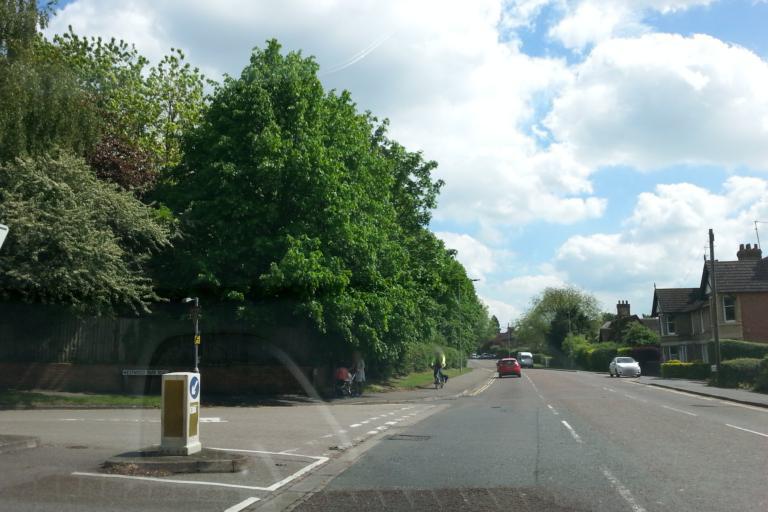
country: GB
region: England
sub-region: Peterborough
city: Peterborough
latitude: 52.5729
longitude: -0.2631
